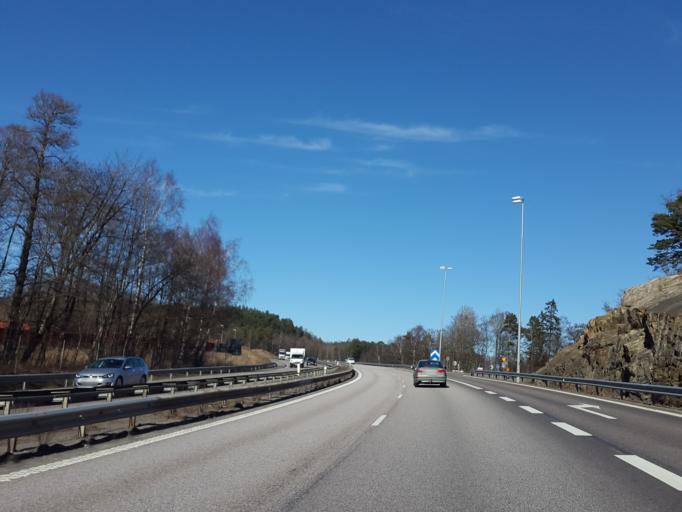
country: SE
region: Vaestra Goetaland
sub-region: Alingsas Kommun
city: Alingsas
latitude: 57.9041
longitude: 12.5006
